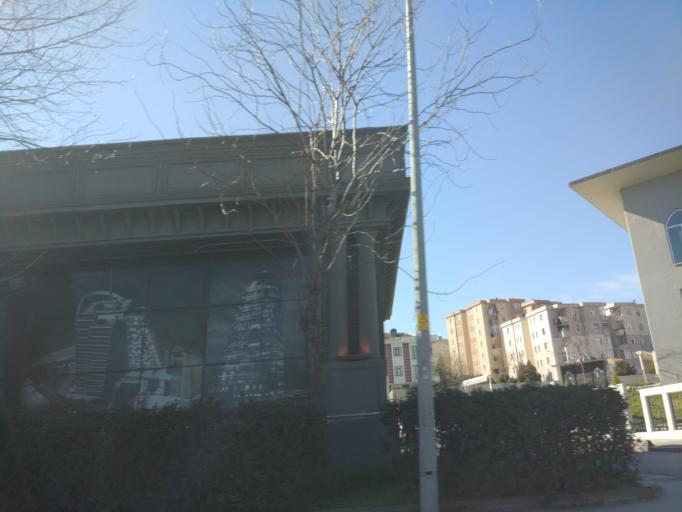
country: TR
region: Istanbul
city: Mahmutbey
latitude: 41.0208
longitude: 28.8054
